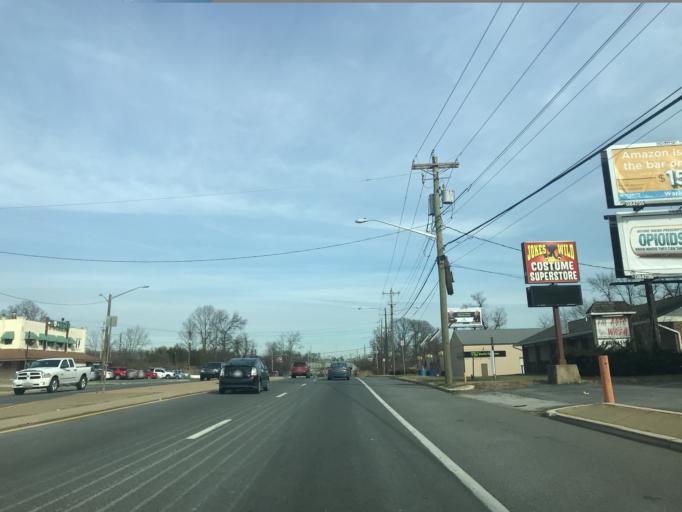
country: US
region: Delaware
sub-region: New Castle County
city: Bear
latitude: 39.6493
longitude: -75.6211
